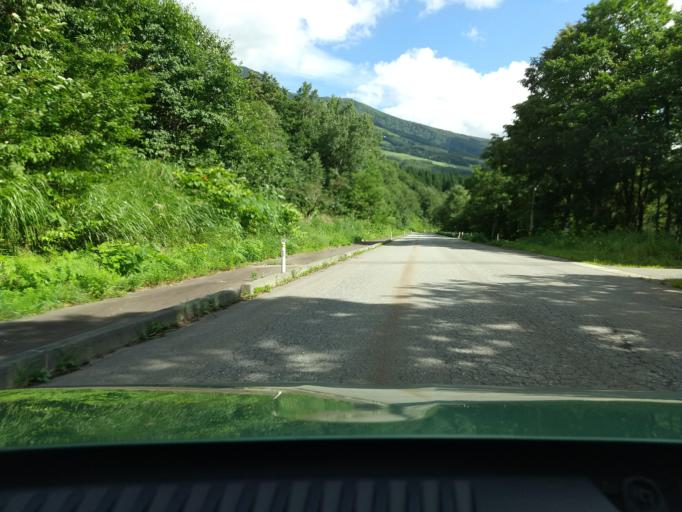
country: JP
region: Iwate
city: Shizukuishi
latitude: 39.7766
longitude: 140.7626
